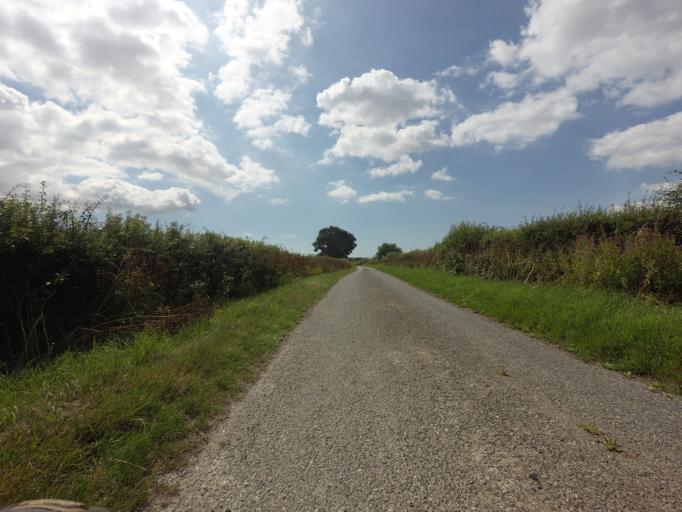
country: GB
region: England
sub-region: Kent
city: Stone
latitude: 51.0519
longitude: 0.7719
